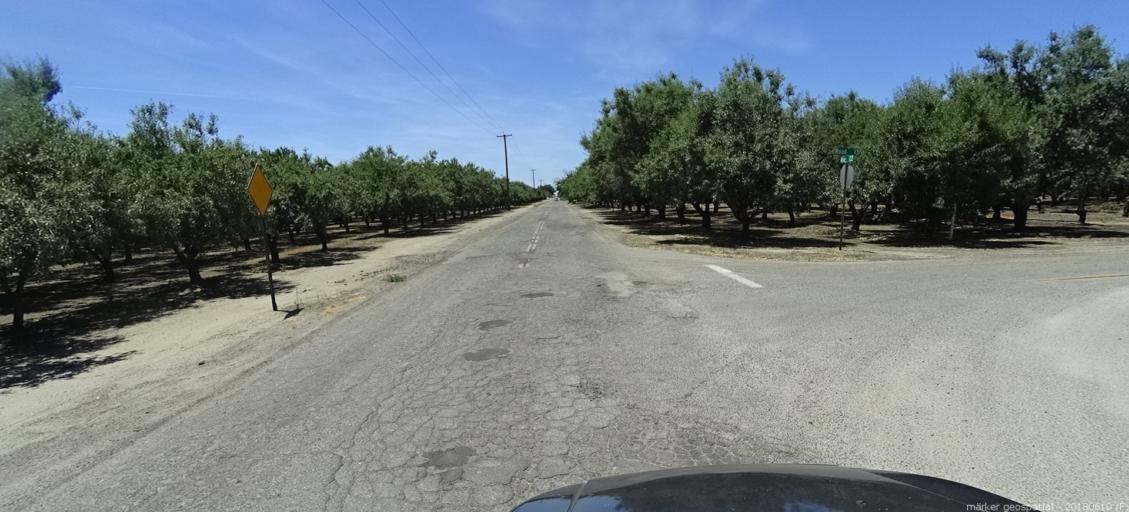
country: US
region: California
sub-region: Madera County
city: Chowchilla
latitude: 37.0690
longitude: -120.3106
